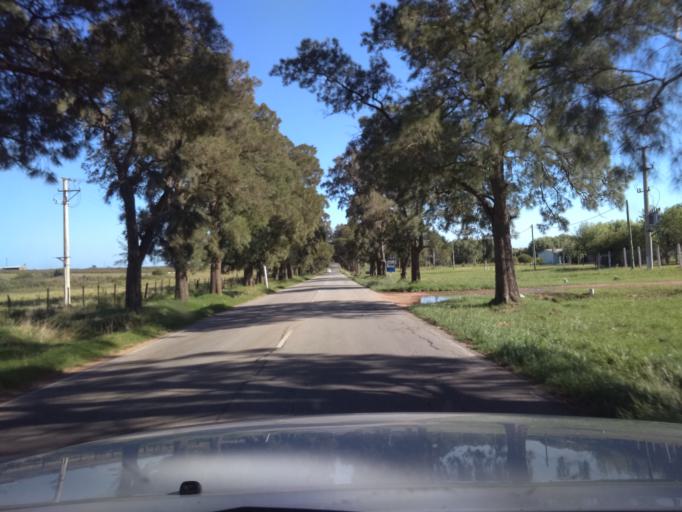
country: UY
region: Canelones
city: San Bautista
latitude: -34.3911
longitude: -55.9596
